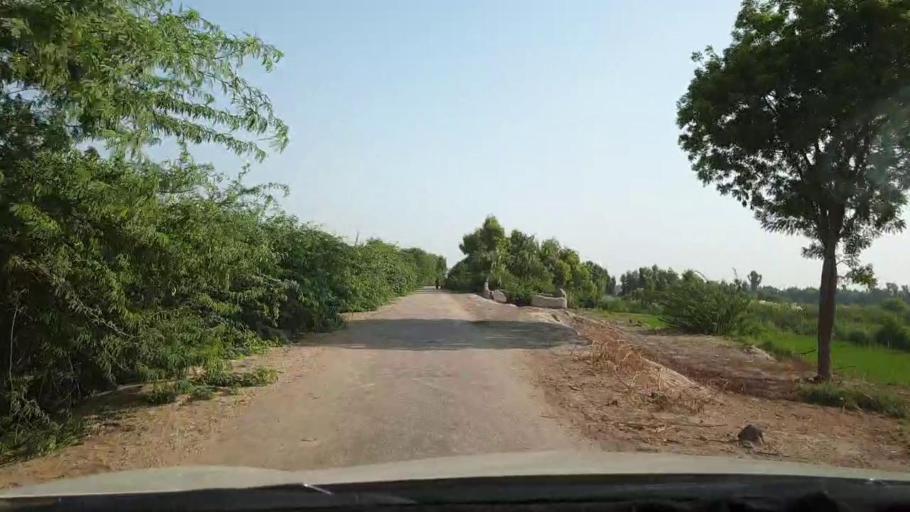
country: PK
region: Sindh
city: Larkana
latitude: 27.5577
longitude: 68.2572
